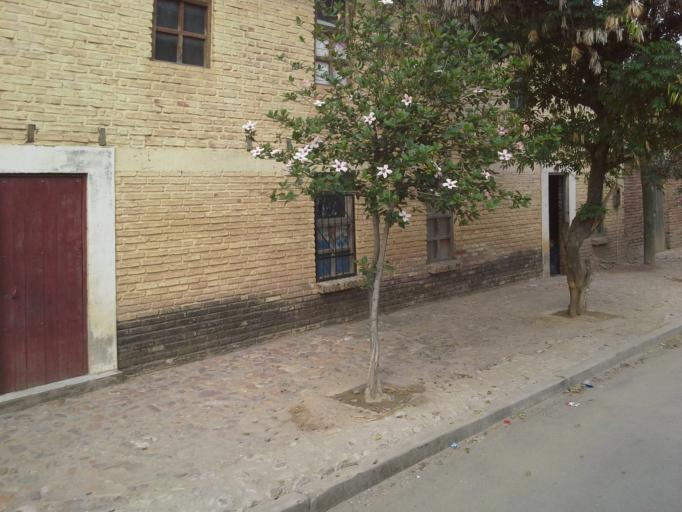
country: BO
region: Cochabamba
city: Tarata
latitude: -17.6101
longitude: -66.0229
